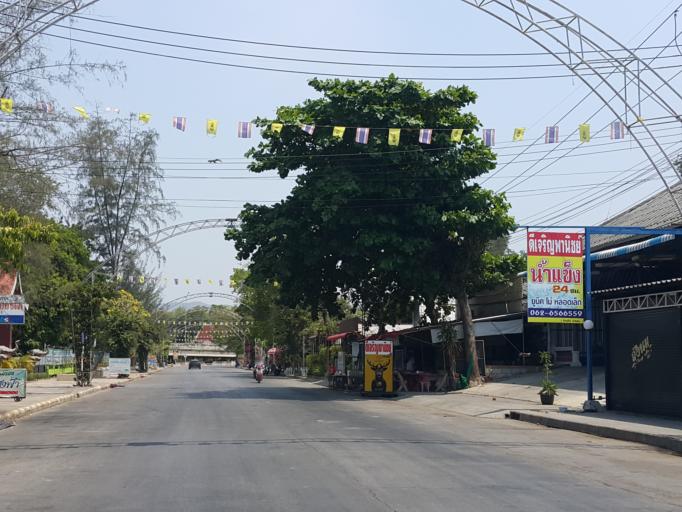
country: TH
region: Kanchanaburi
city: Kanchanaburi
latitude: 14.0235
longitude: 99.5266
